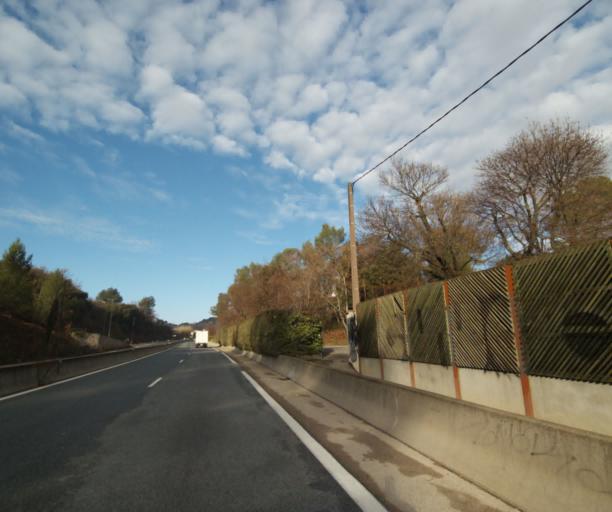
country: FR
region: Provence-Alpes-Cote d'Azur
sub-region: Departement du Var
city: Trans-en-Provence
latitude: 43.4979
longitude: 6.4892
